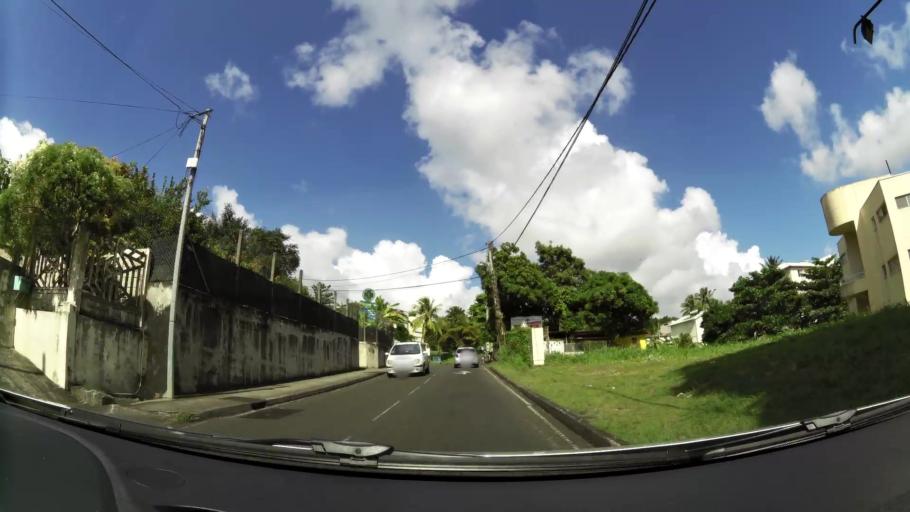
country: MQ
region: Martinique
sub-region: Martinique
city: Fort-de-France
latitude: 14.6176
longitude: -61.0571
